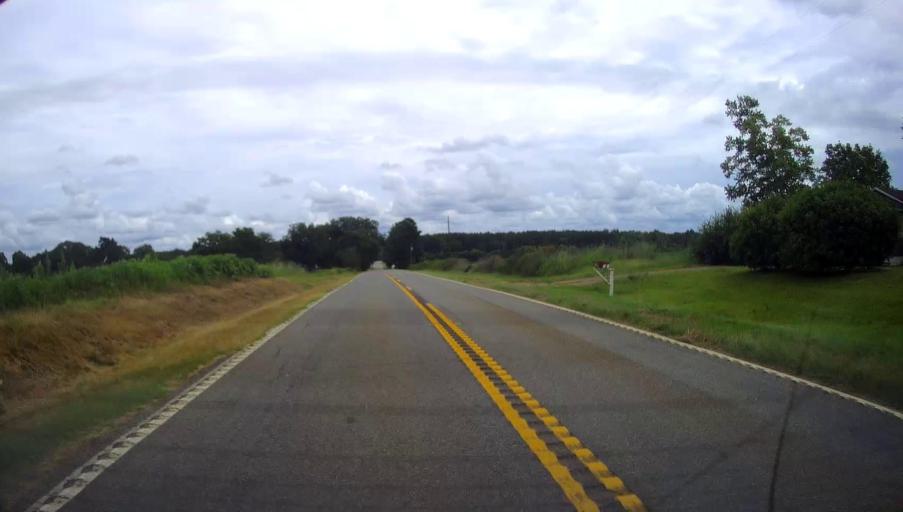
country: US
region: Georgia
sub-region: Macon County
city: Montezuma
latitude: 32.2946
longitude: -83.9024
